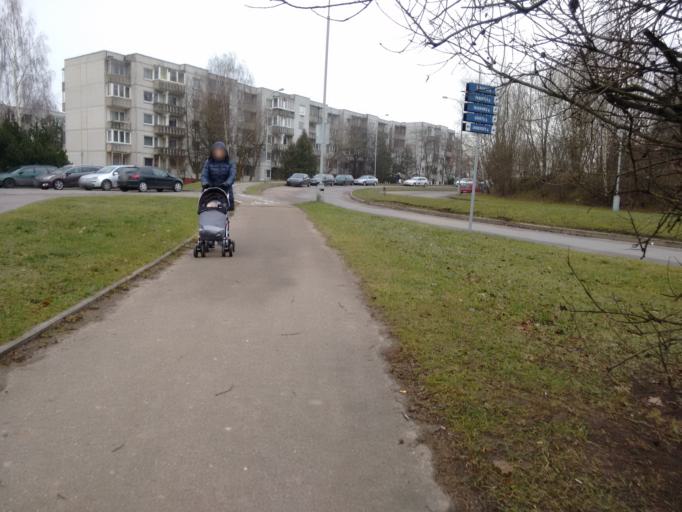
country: LT
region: Vilnius County
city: Seskine
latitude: 54.7182
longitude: 25.2467
